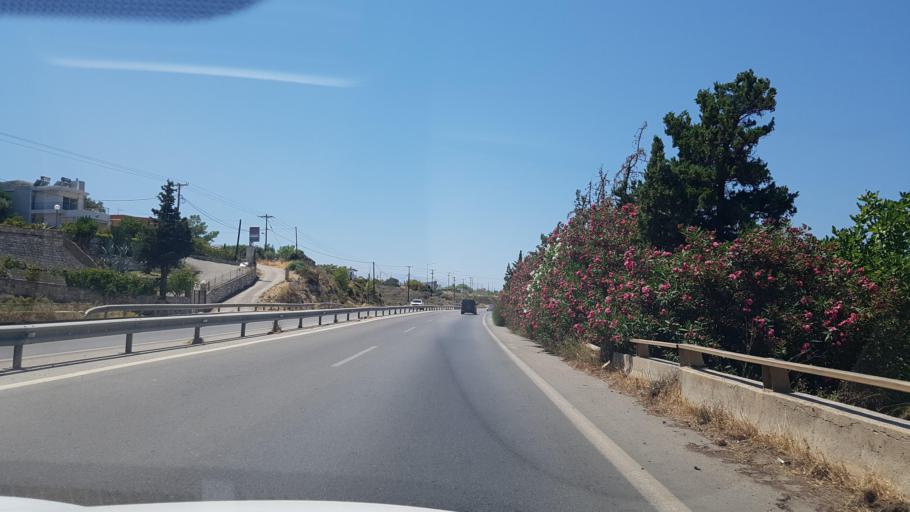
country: GR
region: Crete
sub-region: Nomos Rethymnis
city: Rethymno
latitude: 35.3557
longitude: 24.4738
